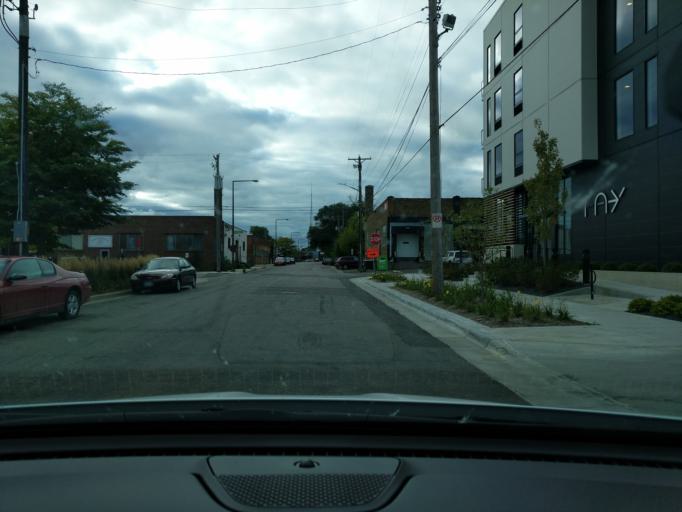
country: US
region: Minnesota
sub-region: Ramsey County
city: Lauderdale
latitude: 44.9641
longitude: -93.1949
